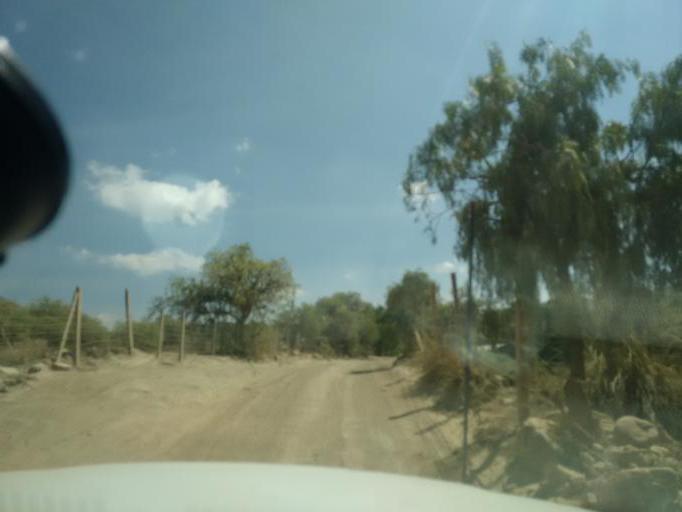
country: CO
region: Boyaca
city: Sachica
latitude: 5.5860
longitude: -73.5308
